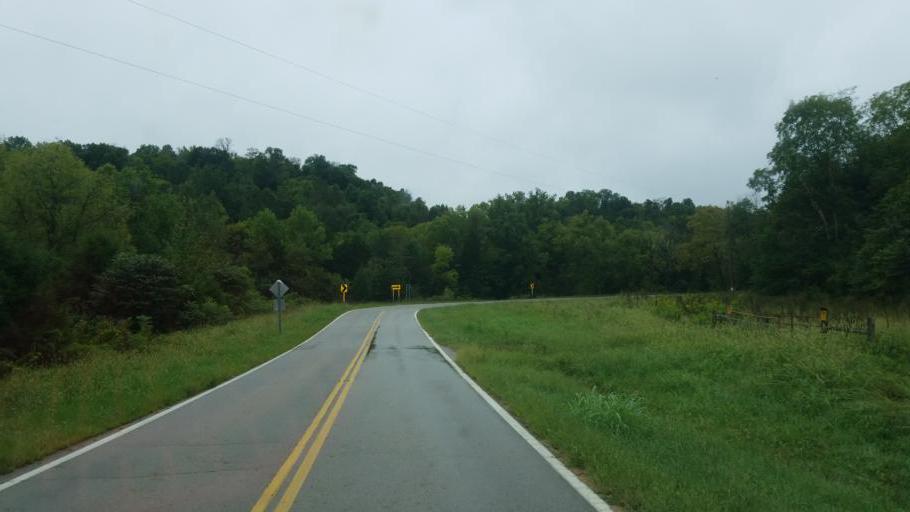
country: US
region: Ohio
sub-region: Adams County
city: West Union
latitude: 38.7488
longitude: -83.5159
